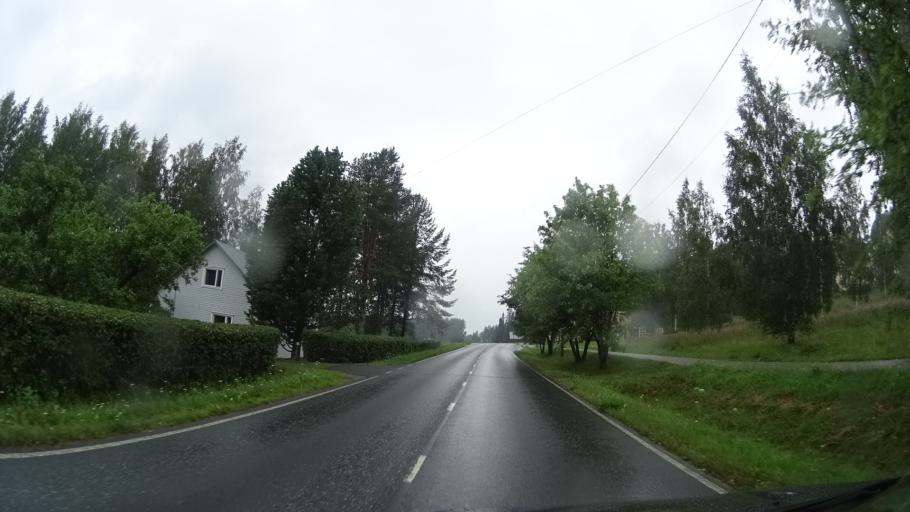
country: FI
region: North Karelia
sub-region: Keski-Karjala
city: Raeaekkylae
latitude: 62.3151
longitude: 29.6206
